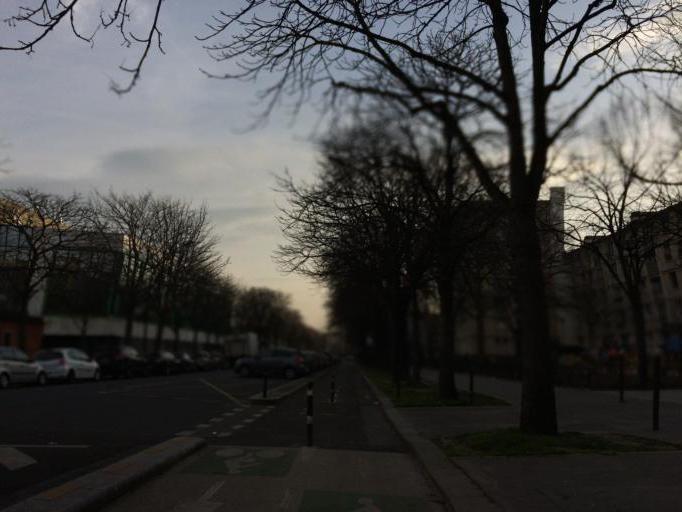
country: FR
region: Ile-de-France
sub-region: Departement du Val-de-Marne
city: Saint-Mande
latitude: 48.8463
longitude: 2.4135
